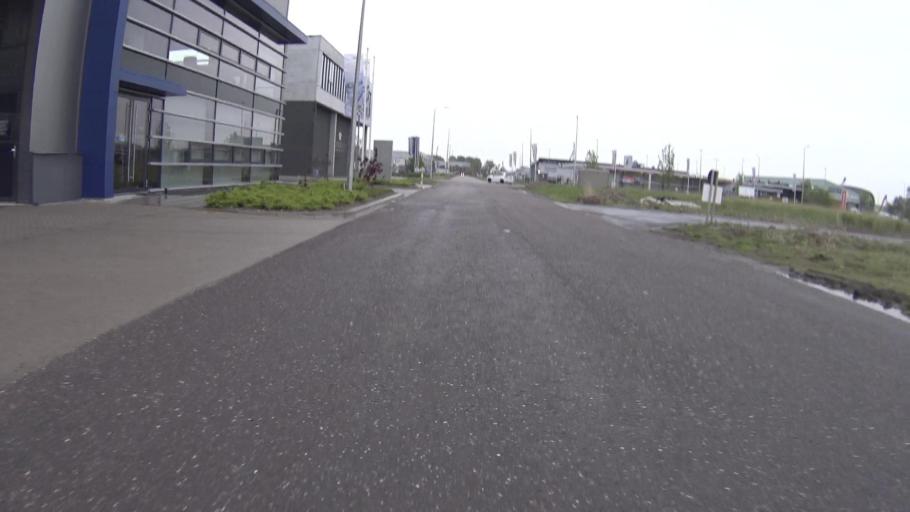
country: NL
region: South Holland
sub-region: Gemeente Brielle
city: Brielle
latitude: 51.8952
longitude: 4.1856
